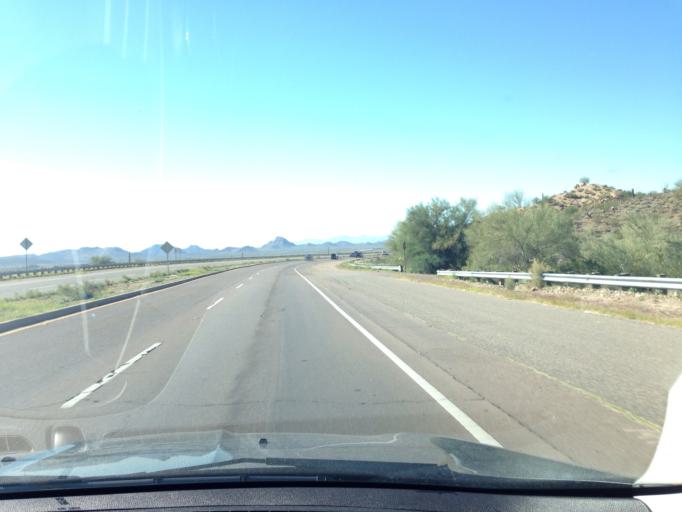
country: US
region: Arizona
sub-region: Maricopa County
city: Anthem
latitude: 33.8000
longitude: -112.0958
